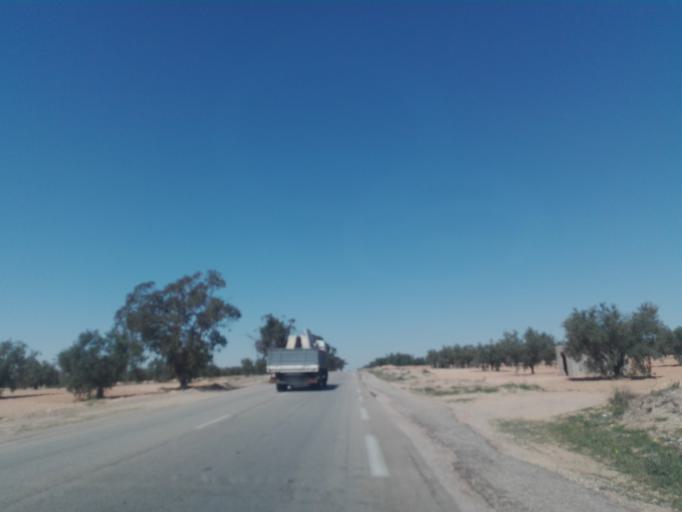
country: TN
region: Safaqis
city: Bi'r `Ali Bin Khalifah
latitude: 34.7581
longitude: 10.3111
